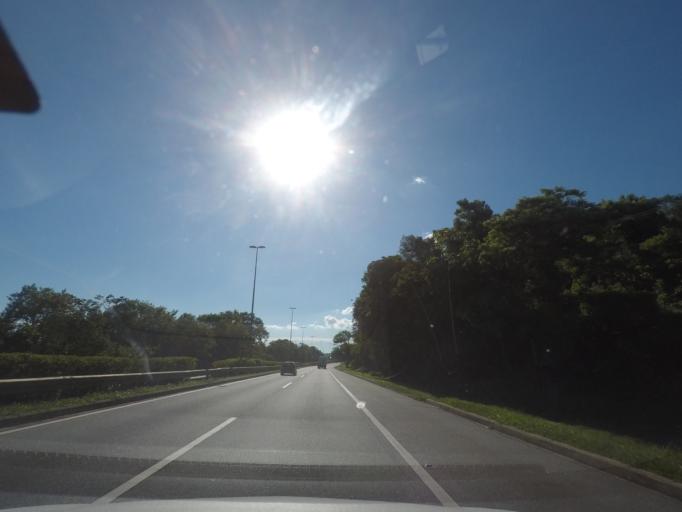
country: BR
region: Rio de Janeiro
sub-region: Sao Goncalo
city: Sao Goncalo
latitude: -22.6656
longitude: -43.1008
